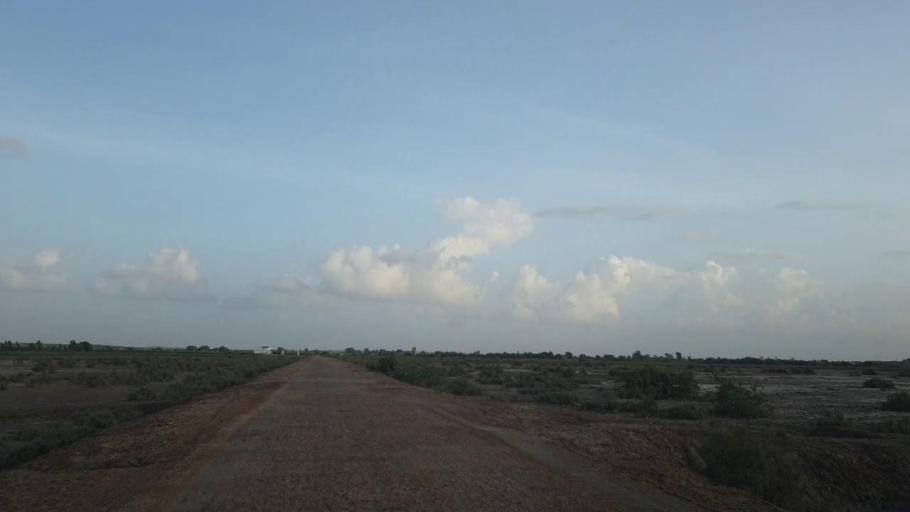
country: PK
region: Sindh
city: Kadhan
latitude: 24.5524
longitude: 69.1236
